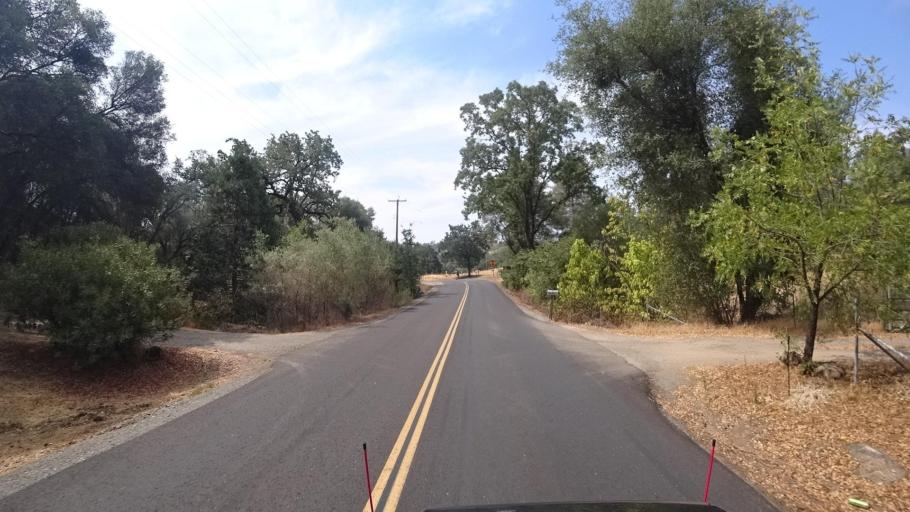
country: US
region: California
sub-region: Mariposa County
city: Mariposa
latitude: 37.4615
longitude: -119.9014
